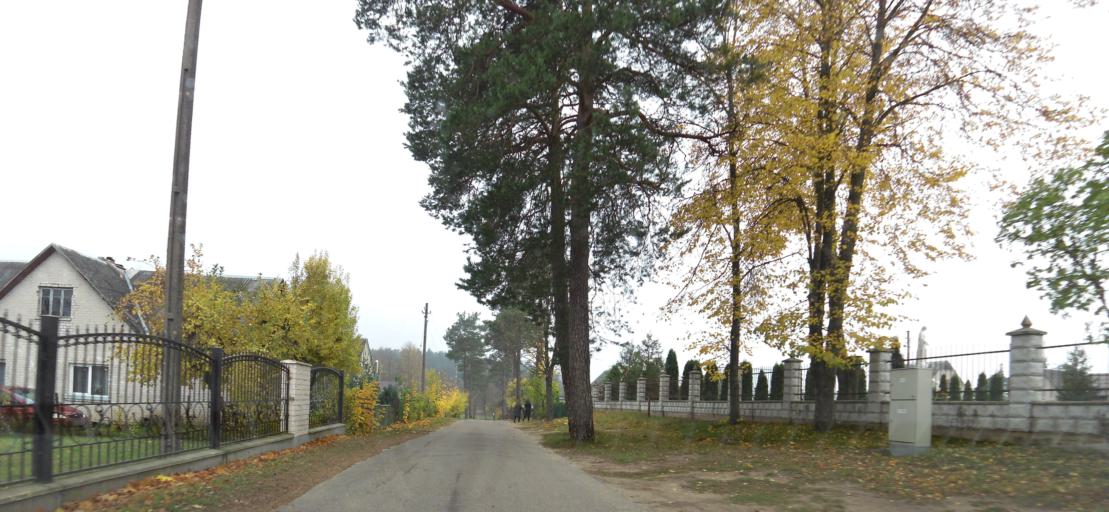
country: BY
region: Grodnenskaya
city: Astravyets
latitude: 54.6360
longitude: 25.6875
